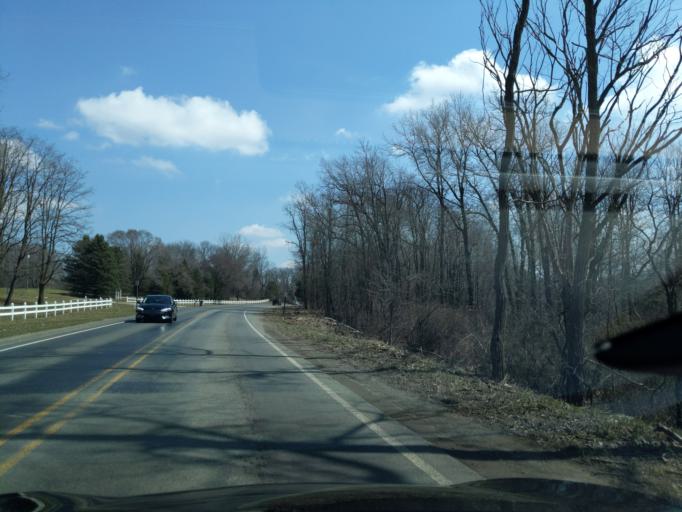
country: US
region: Michigan
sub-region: Calhoun County
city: Marshall
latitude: 42.3492
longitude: -84.9925
